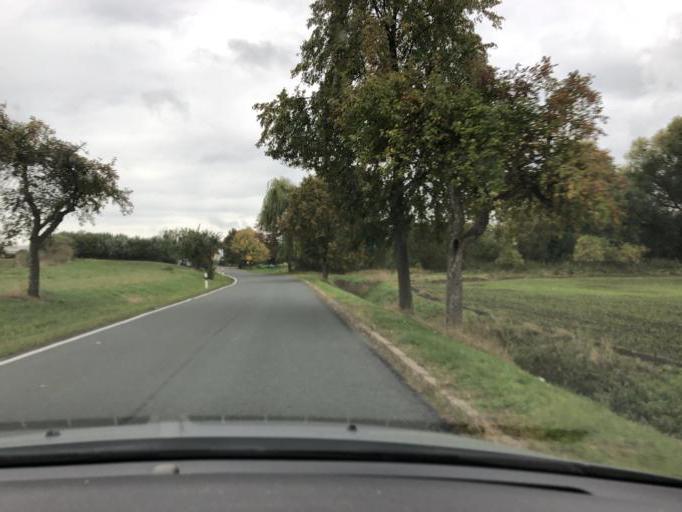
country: DE
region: Saxony-Anhalt
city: Goseck
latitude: 51.2016
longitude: 11.8706
